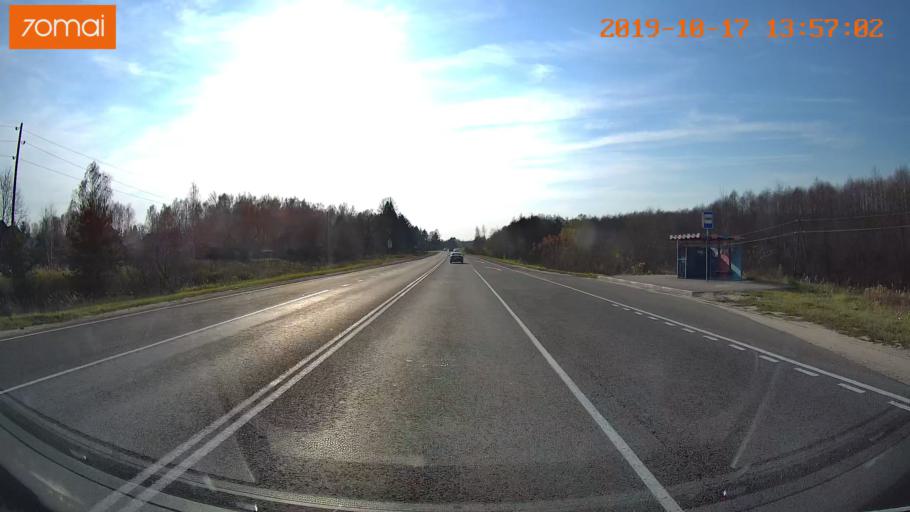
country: RU
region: Rjazan
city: Spas-Klepiki
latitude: 55.1473
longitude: 40.2541
